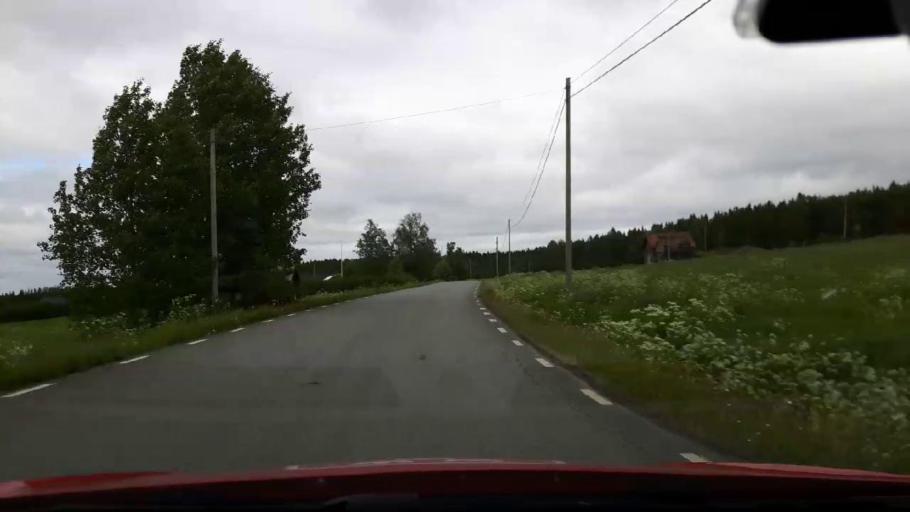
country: SE
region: Jaemtland
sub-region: Krokoms Kommun
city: Krokom
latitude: 63.2566
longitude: 14.5361
